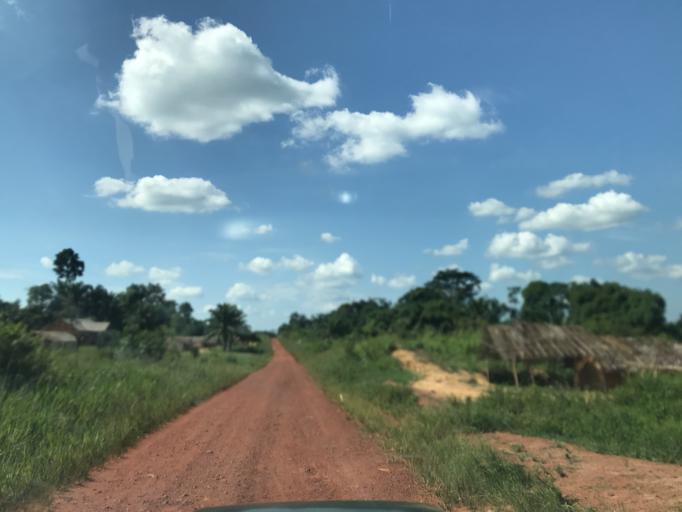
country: CD
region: Eastern Province
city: Kisangani
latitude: 1.2168
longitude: 25.2674
